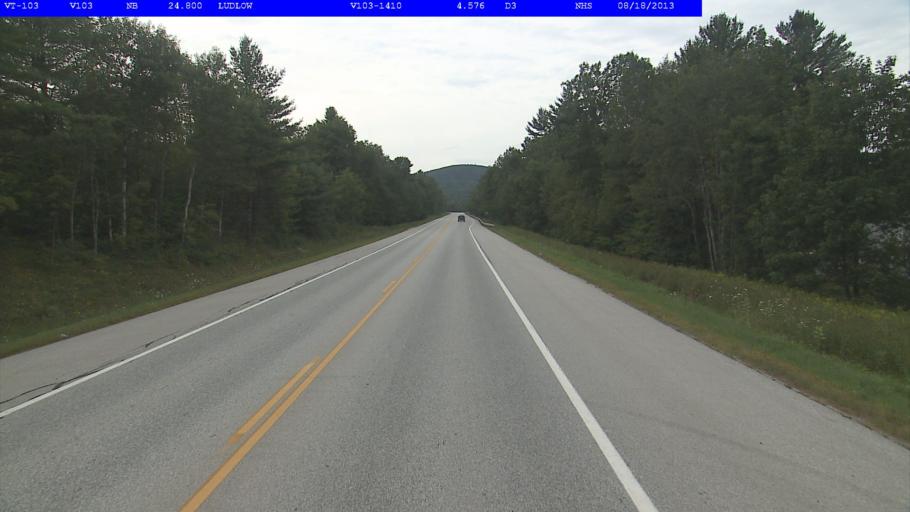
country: US
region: Vermont
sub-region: Windsor County
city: Chester
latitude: 43.4256
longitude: -72.7138
